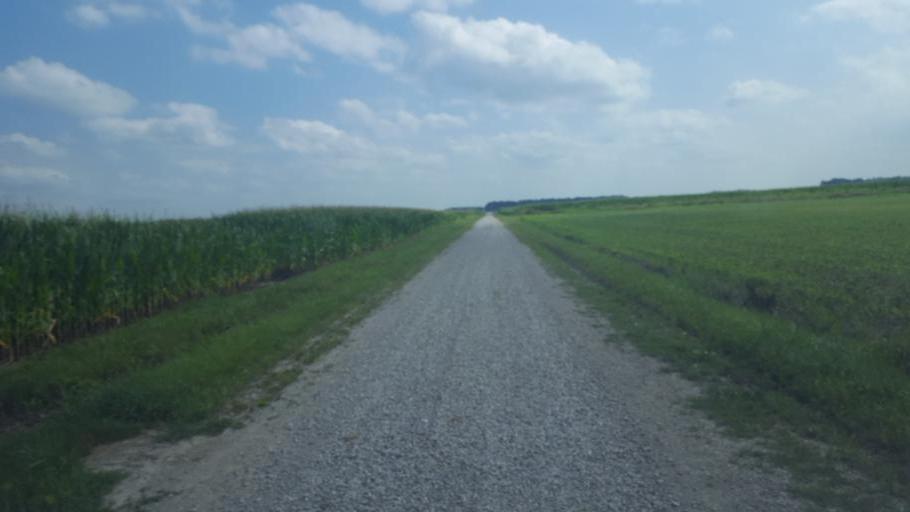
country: US
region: Ohio
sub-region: Huron County
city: Willard
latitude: 40.9914
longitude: -82.7625
